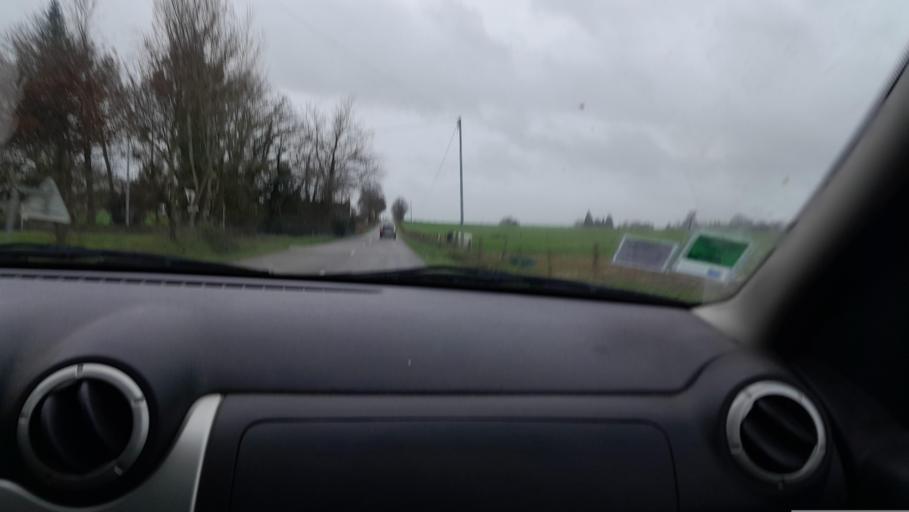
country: FR
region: Pays de la Loire
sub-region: Departement de la Mayenne
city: Ballots
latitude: 47.9286
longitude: -1.0922
